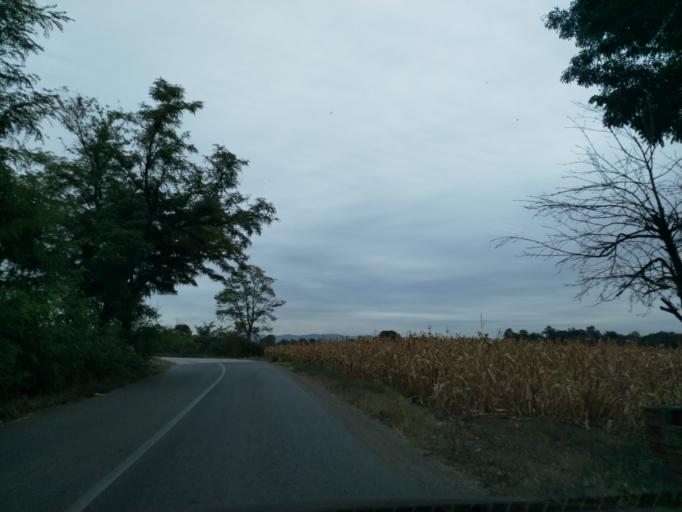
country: RS
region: Central Serbia
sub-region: Pomoravski Okrug
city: Paracin
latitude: 43.8361
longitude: 21.3687
